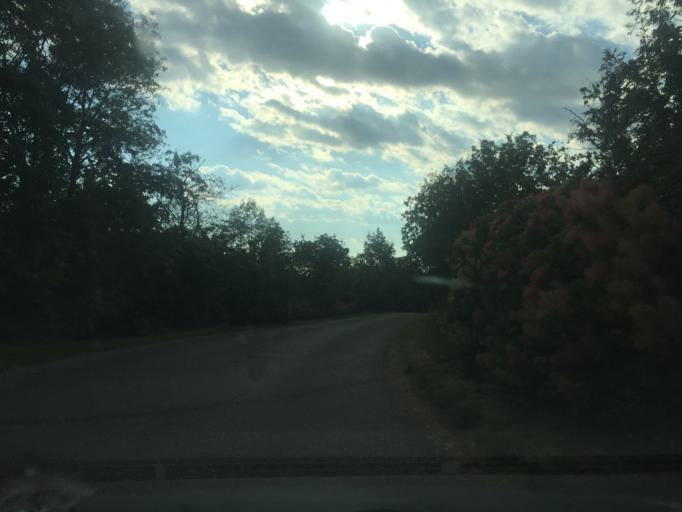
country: IT
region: Friuli Venezia Giulia
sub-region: Provincia di Gorizia
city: Doberdo del Lago
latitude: 45.8751
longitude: 13.5430
